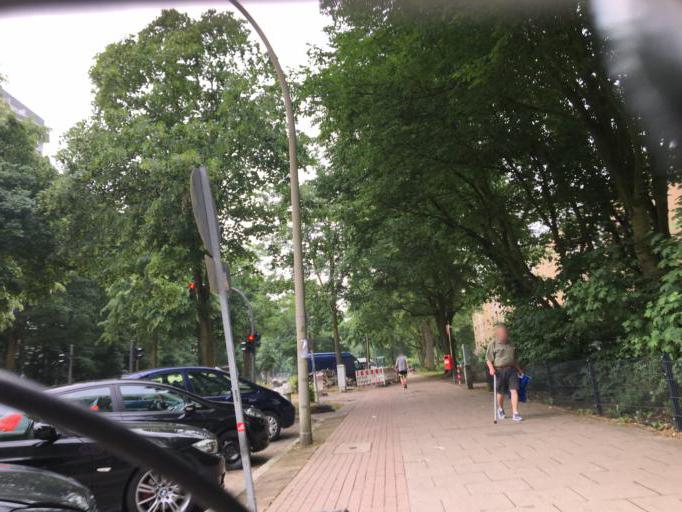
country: DE
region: Schleswig-Holstein
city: Halstenbek
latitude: 53.5863
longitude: 9.8515
